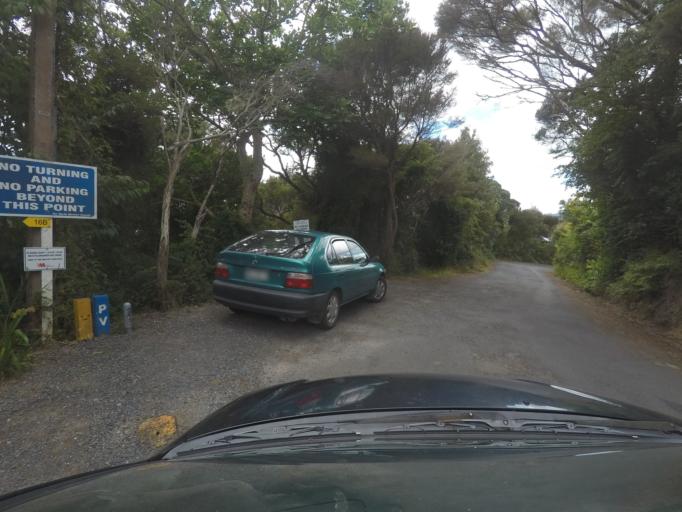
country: NZ
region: Northland
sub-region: Far North District
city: Paihia
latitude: -35.2884
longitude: 174.0979
